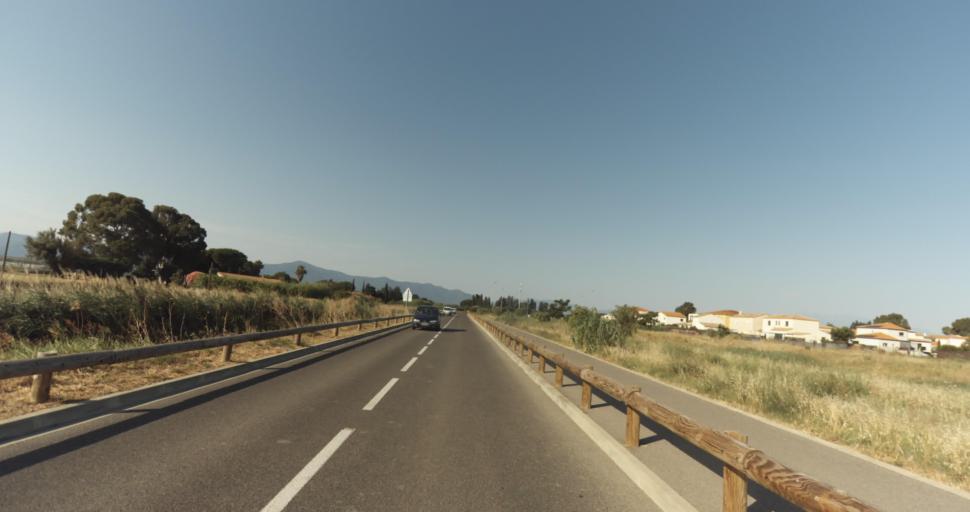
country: FR
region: Languedoc-Roussillon
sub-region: Departement des Pyrenees-Orientales
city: Alenya
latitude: 42.6371
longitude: 2.9909
